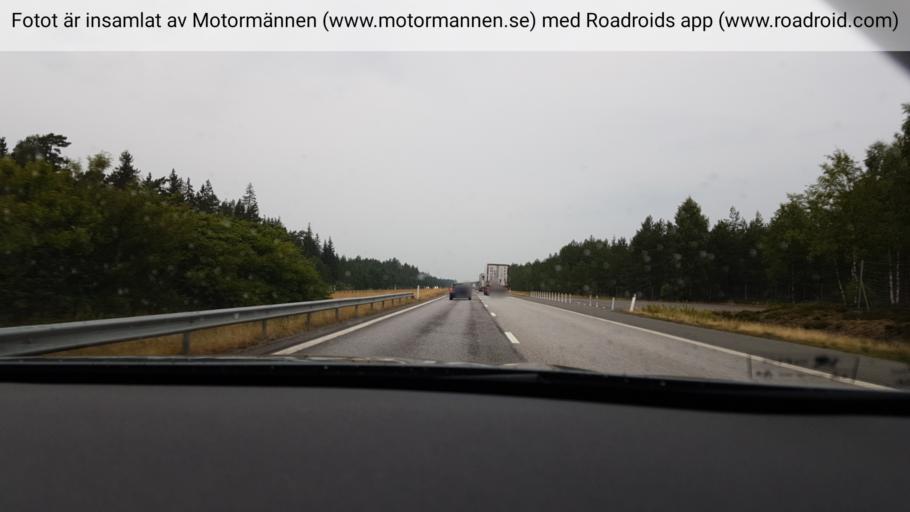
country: SE
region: Joenkoeping
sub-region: Varnamo Kommun
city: Varnamo
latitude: 57.3039
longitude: 14.0923
